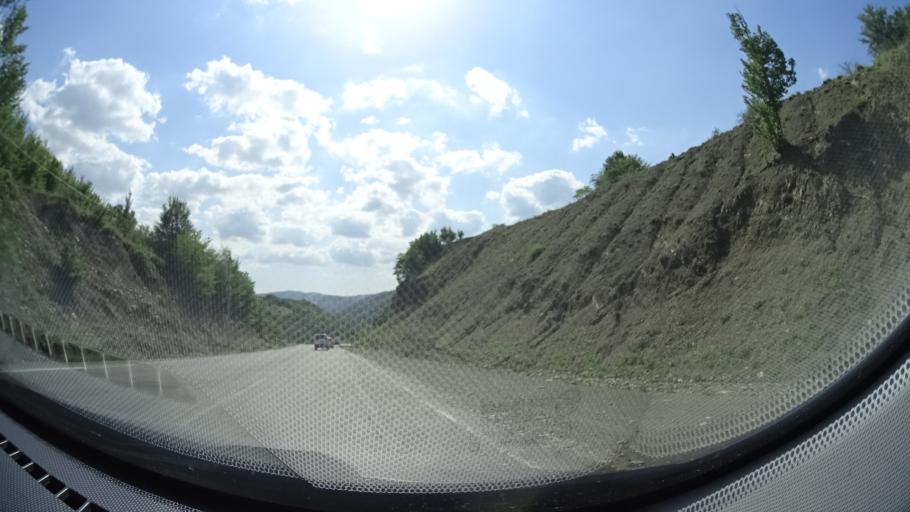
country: GE
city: Zhinvali
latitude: 42.1599
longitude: 44.7148
